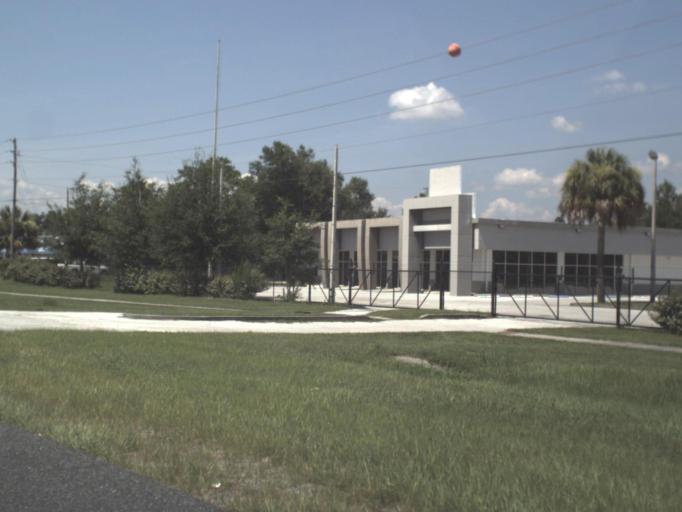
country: US
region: Florida
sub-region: Citrus County
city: Crystal River
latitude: 28.8746
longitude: -82.5798
